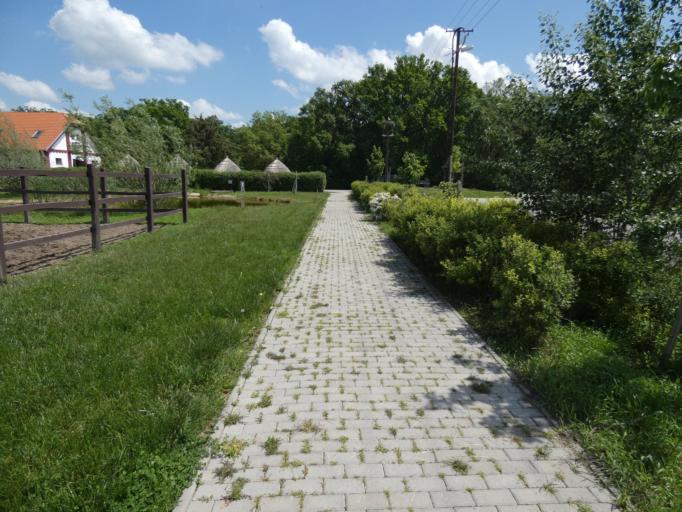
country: HU
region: Hajdu-Bihar
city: Hortobagy
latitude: 47.5943
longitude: 21.1558
